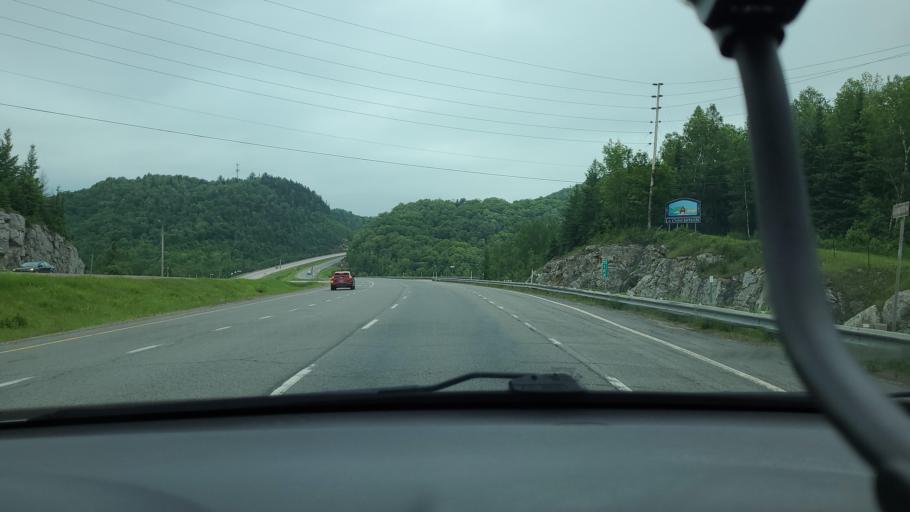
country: CA
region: Quebec
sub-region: Laurentides
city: Mont-Tremblant
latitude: 46.1437
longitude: -74.6519
